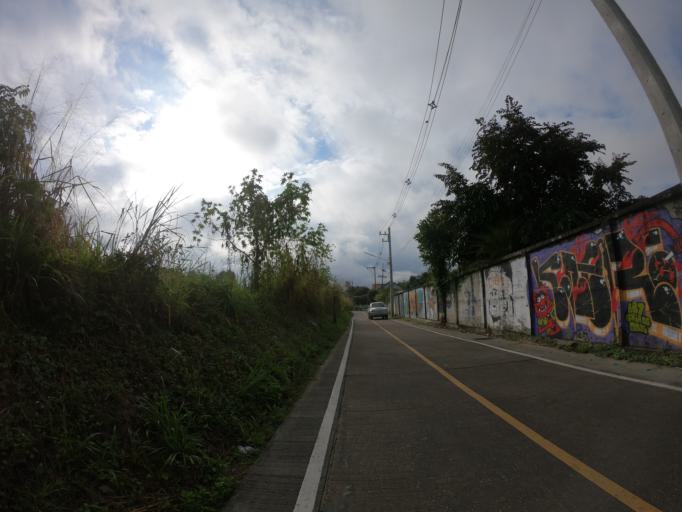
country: TH
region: Chiang Mai
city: Chiang Mai
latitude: 18.8166
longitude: 98.9648
